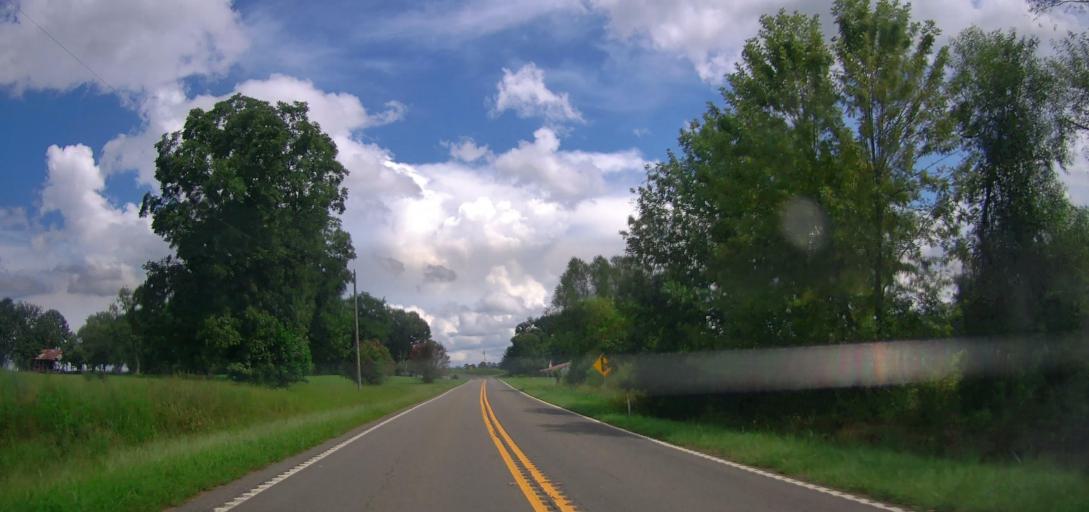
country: US
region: Georgia
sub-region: Taylor County
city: Reynolds
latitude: 32.4409
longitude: -84.1079
